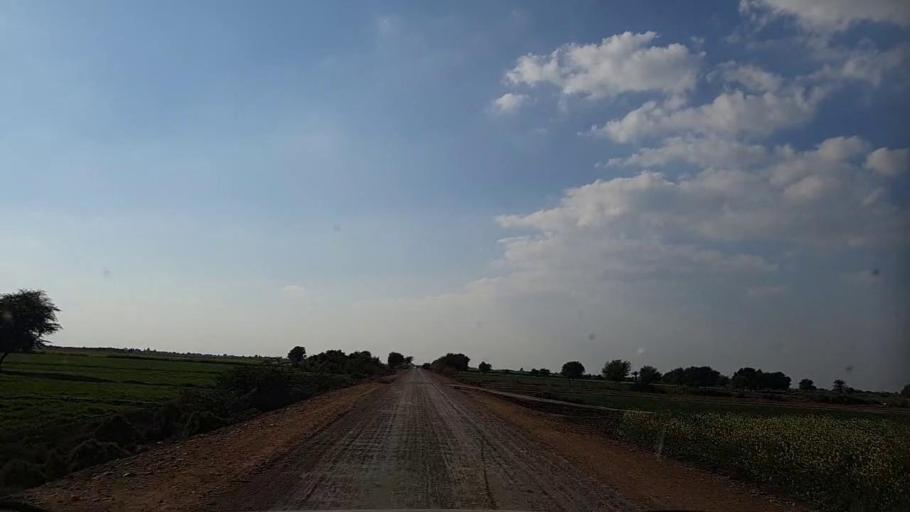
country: PK
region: Sindh
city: Pithoro
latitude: 25.6516
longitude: 69.2586
